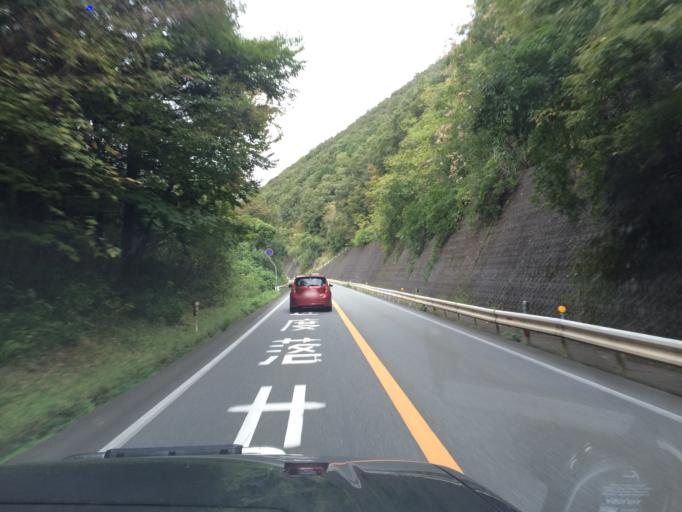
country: JP
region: Hyogo
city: Toyooka
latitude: 35.3678
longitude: 134.8220
